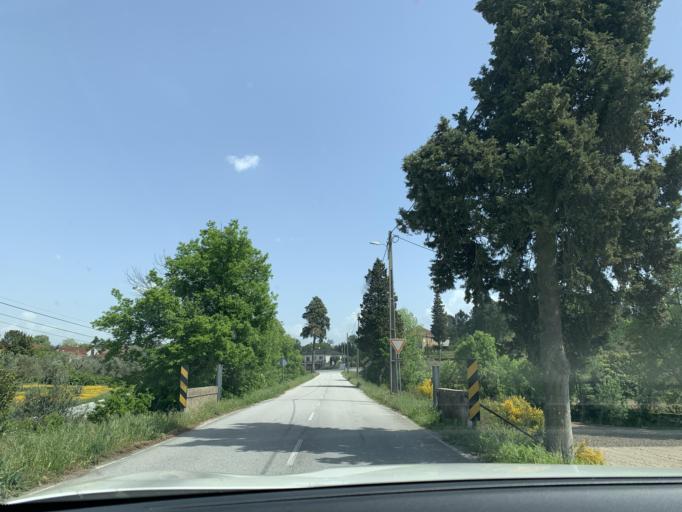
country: PT
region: Guarda
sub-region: Fornos de Algodres
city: Fornos de Algodres
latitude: 40.5792
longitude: -7.6114
